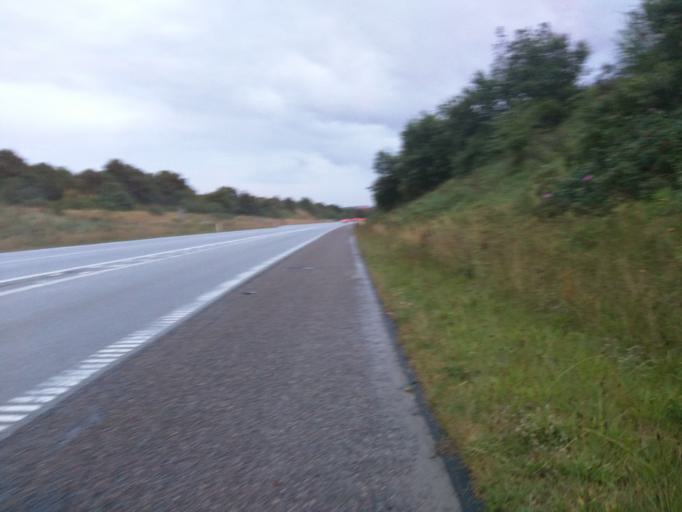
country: DK
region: Central Jutland
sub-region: Viborg Kommune
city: Viborg
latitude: 56.4357
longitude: 9.3851
